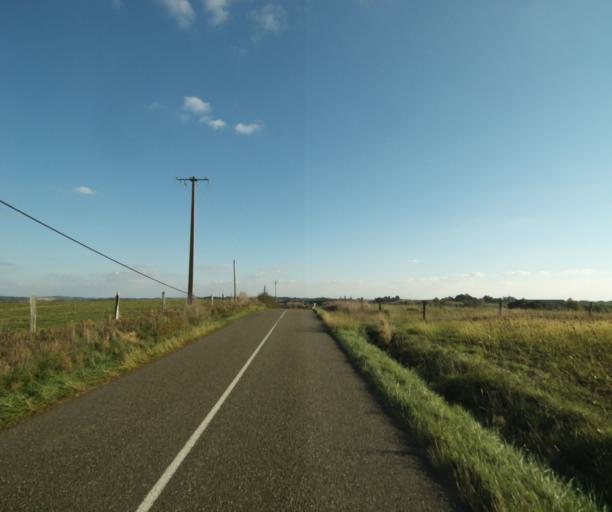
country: FR
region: Midi-Pyrenees
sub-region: Departement du Gers
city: Eauze
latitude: 43.7580
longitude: 0.1316
